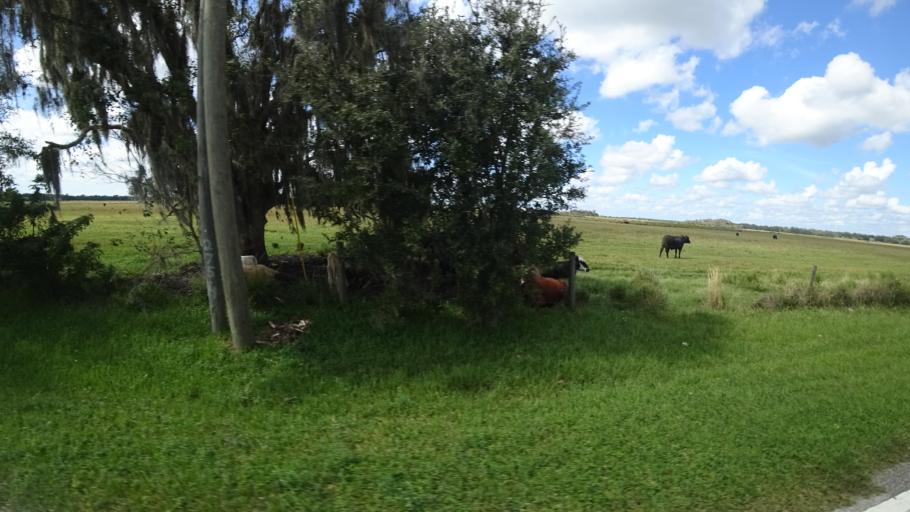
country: US
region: Florida
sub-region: Sarasota County
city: Lake Sarasota
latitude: 27.3417
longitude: -82.2693
